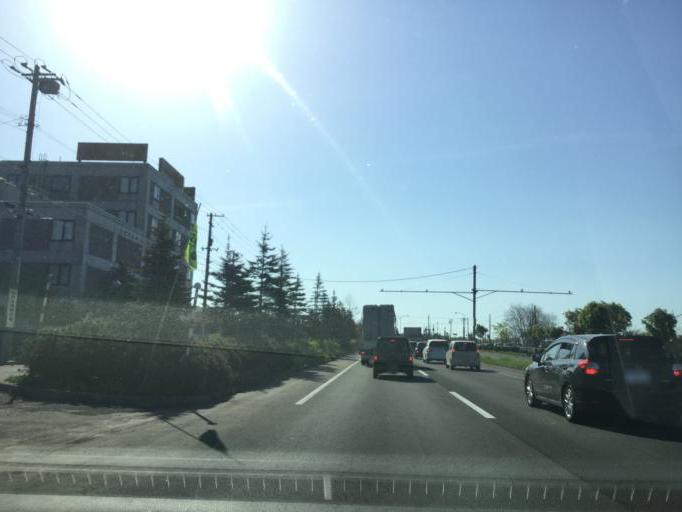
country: JP
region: Hokkaido
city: Kitahiroshima
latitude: 43.0132
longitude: 141.5049
